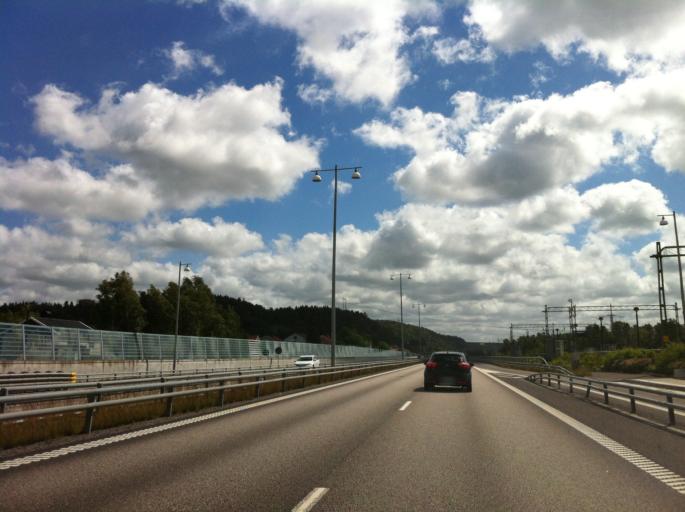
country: SE
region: Vaestra Goetaland
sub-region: Ale Kommun
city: Surte
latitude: 57.8646
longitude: 12.0207
